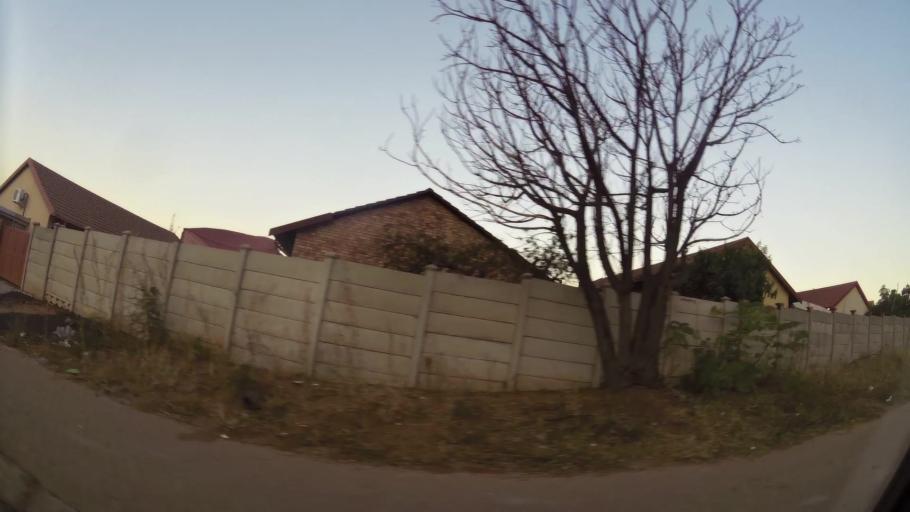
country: ZA
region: North-West
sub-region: Bojanala Platinum District Municipality
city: Rustenburg
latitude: -25.6518
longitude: 27.2020
